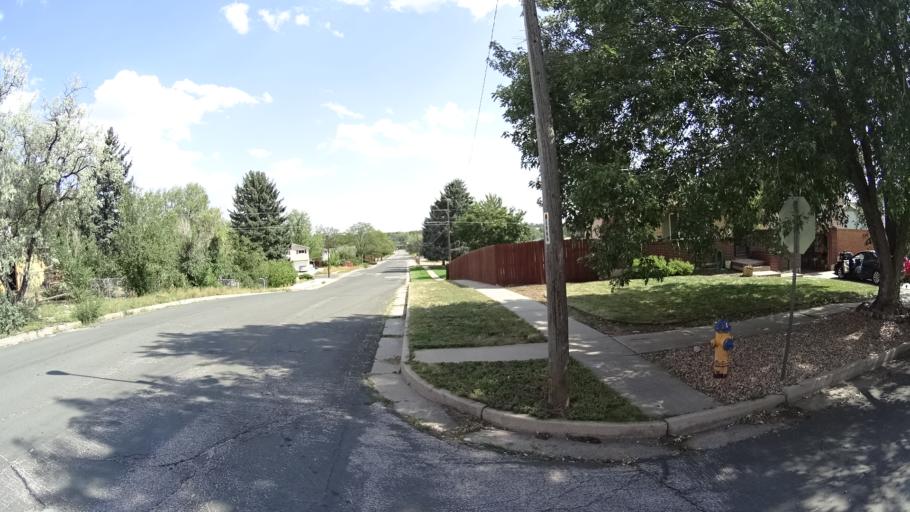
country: US
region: Colorado
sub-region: El Paso County
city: Colorado Springs
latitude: 38.8527
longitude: -104.7683
